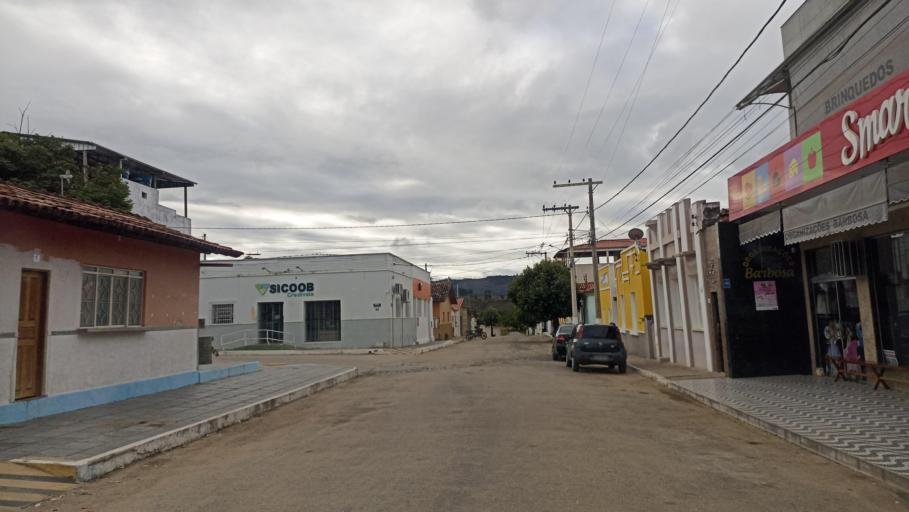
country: BR
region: Minas Gerais
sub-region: Almenara
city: Almenara
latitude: -16.6087
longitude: -40.5695
